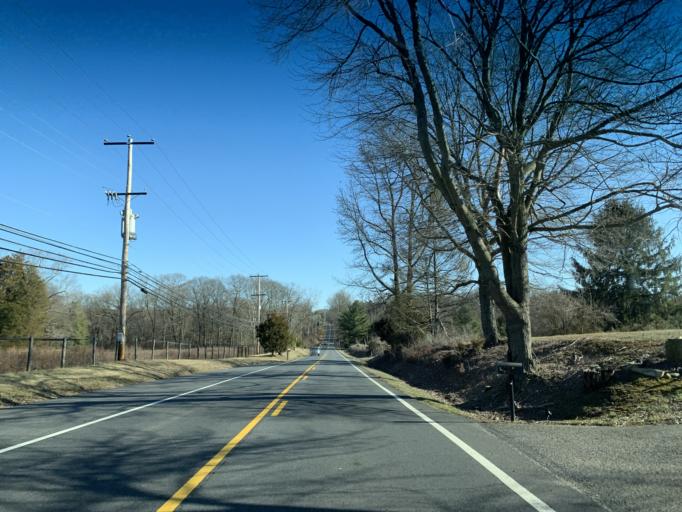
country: US
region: Maryland
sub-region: Cecil County
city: Elkton
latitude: 39.6563
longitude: -75.8848
